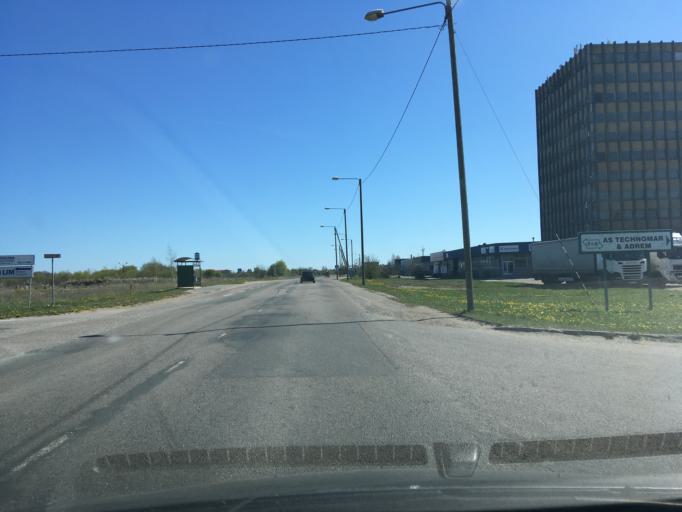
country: EE
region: Harju
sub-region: Joelaehtme vald
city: Loo
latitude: 59.4566
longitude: 24.9439
